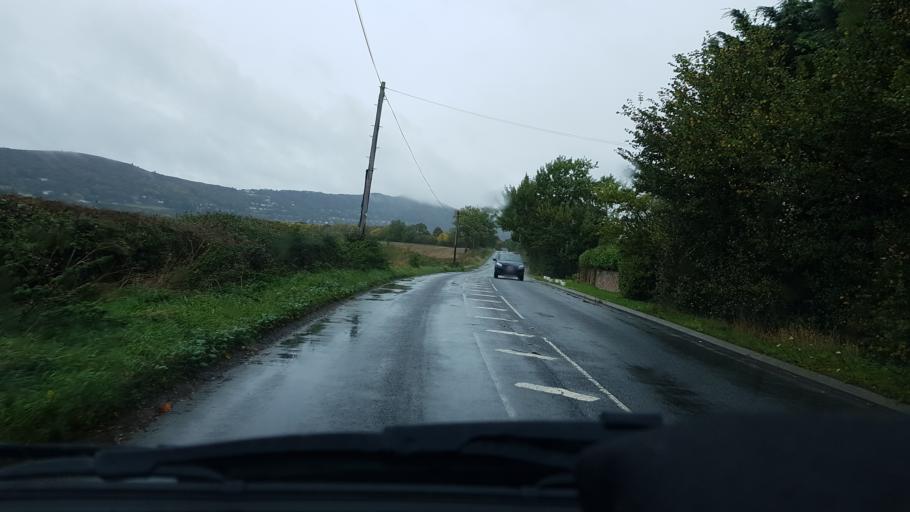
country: GB
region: England
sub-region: Worcestershire
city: Great Malvern
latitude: 52.0719
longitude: -2.3006
